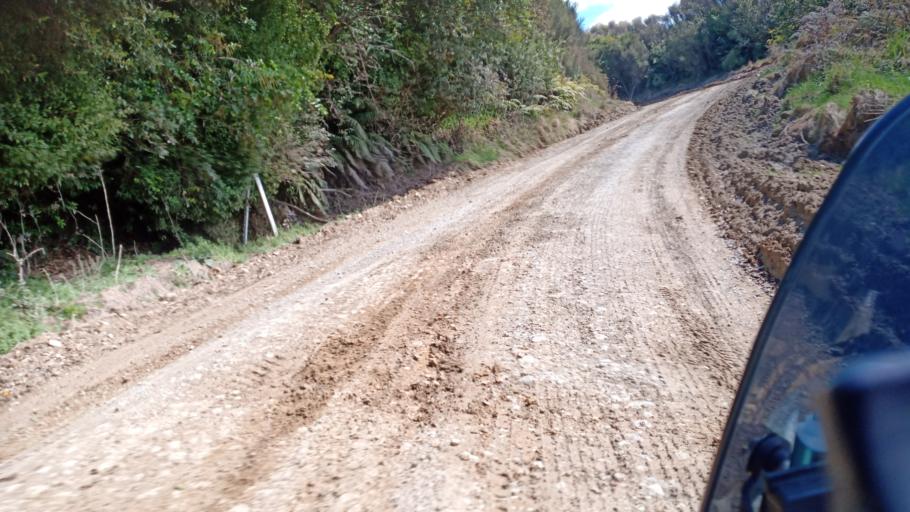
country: NZ
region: Gisborne
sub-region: Gisborne District
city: Gisborne
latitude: -38.8747
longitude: 177.7876
